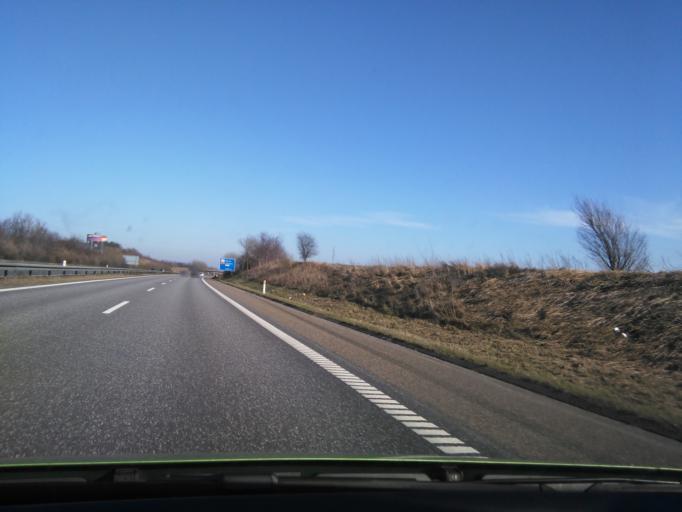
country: DK
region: Zealand
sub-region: Soro Kommune
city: Soro
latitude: 55.4564
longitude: 11.5415
